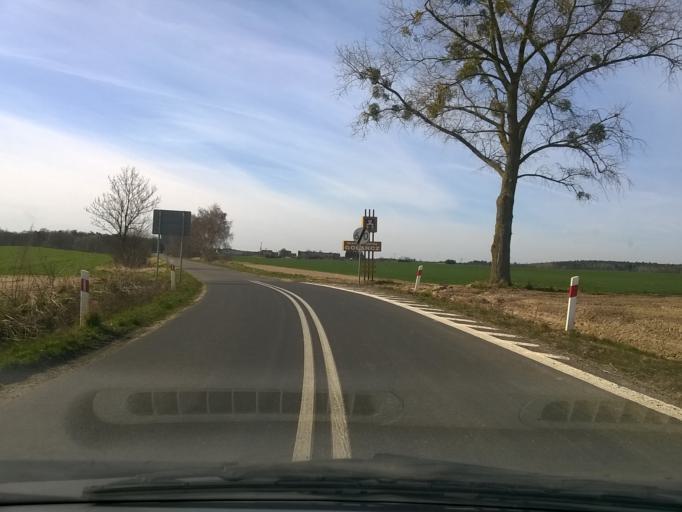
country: PL
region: Greater Poland Voivodeship
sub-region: Powiat wagrowiecki
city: Golancz
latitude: 53.0323
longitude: 17.3358
